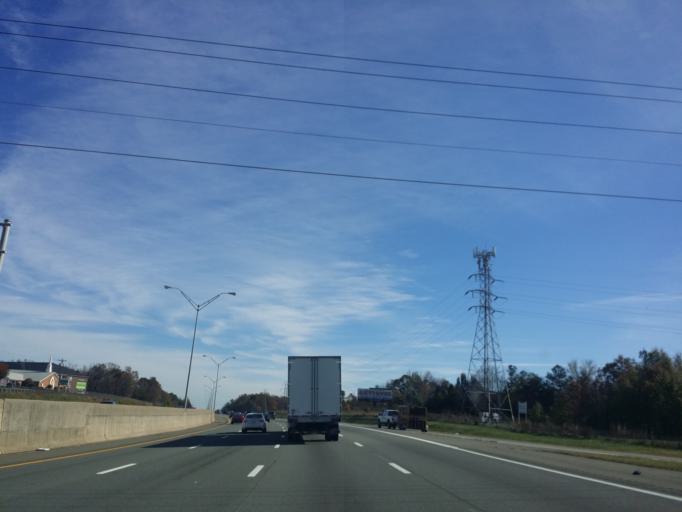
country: US
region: North Carolina
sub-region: Alamance County
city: Burlington
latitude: 36.0645
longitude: -79.4662
